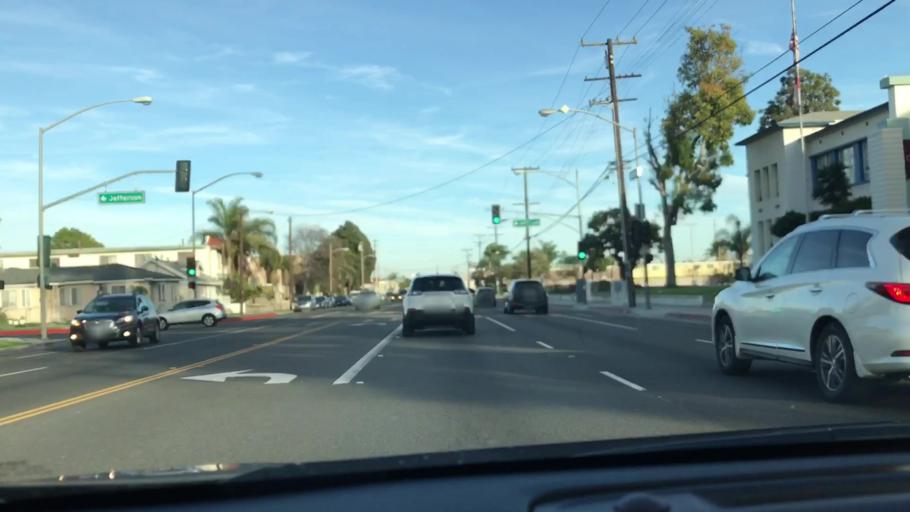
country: US
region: California
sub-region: Los Angeles County
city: Lawndale
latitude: 33.9018
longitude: -118.3472
